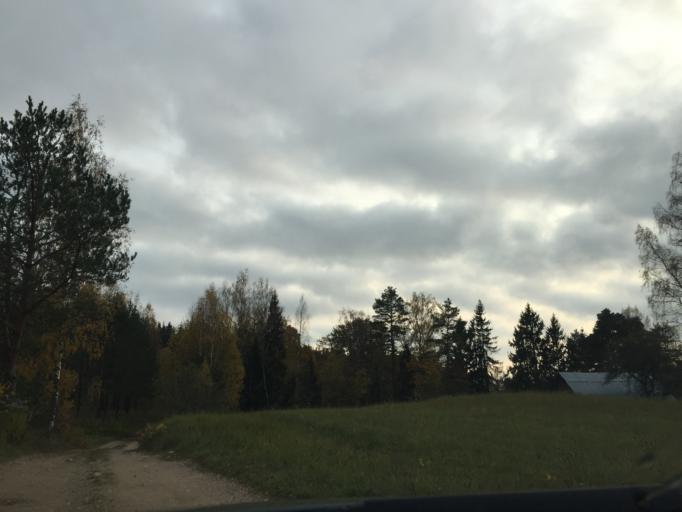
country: LV
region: Pargaujas
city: Stalbe
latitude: 57.3341
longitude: 25.1510
